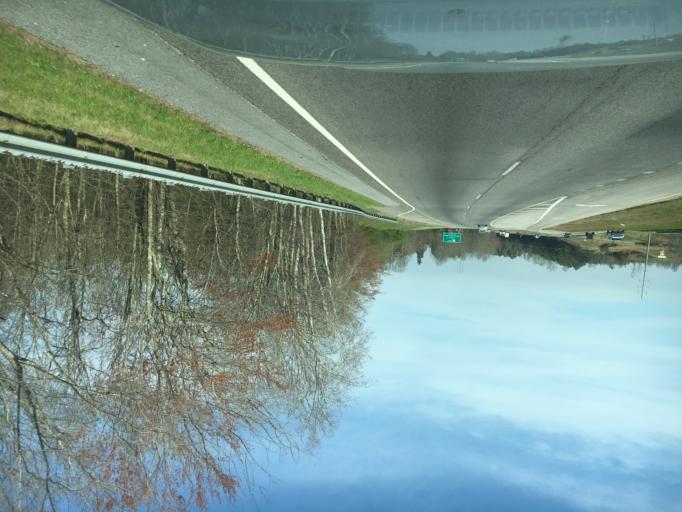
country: US
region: Georgia
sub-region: Banks County
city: Alto
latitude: 34.4890
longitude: -83.5804
